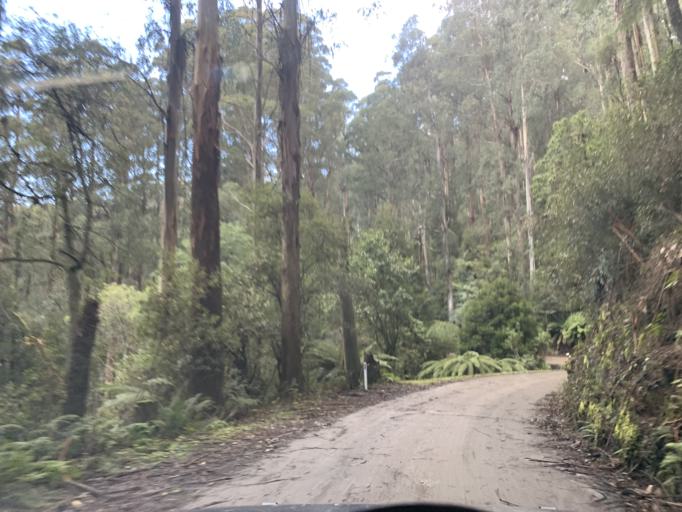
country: AU
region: Victoria
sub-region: Yarra Ranges
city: Millgrove
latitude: -37.6958
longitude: 145.7218
